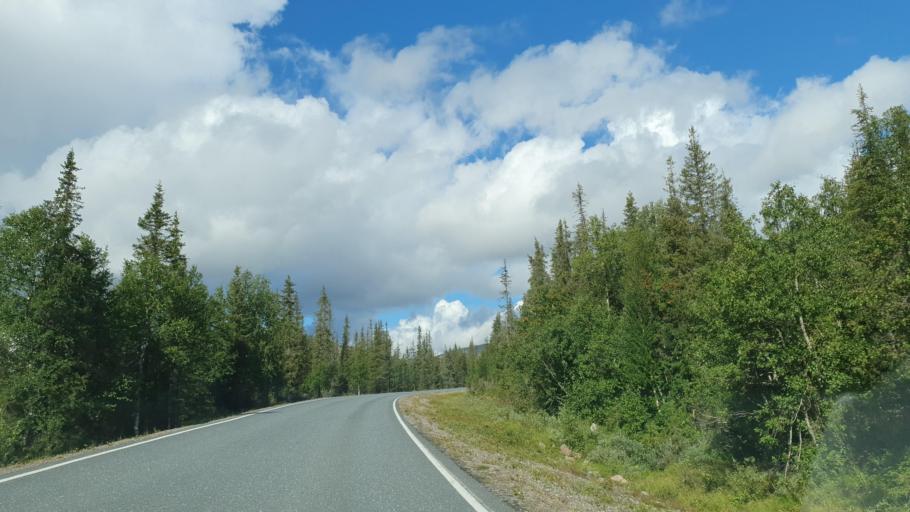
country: FI
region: Lapland
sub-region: Tunturi-Lappi
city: Muonio
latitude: 68.0357
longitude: 24.0665
